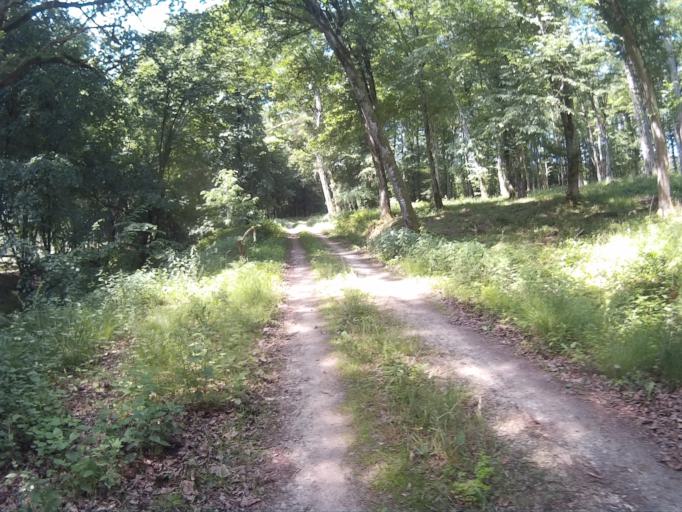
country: AT
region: Burgenland
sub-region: Politischer Bezirk Gussing
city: Heiligenbrunn
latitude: 46.8983
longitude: 16.4441
